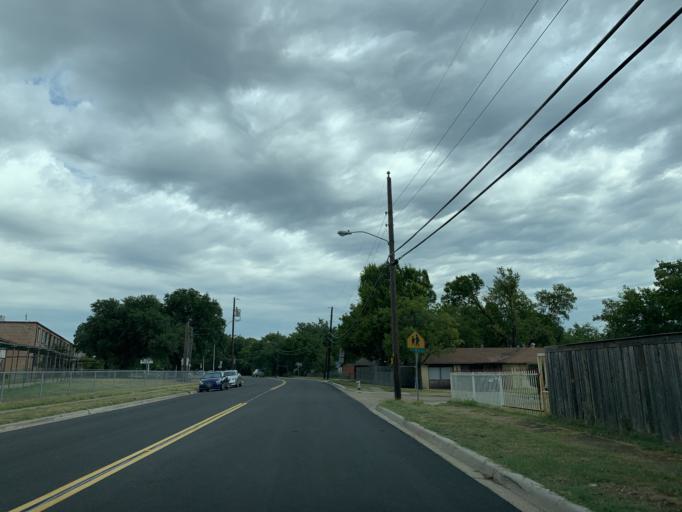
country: US
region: Texas
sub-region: Dallas County
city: Duncanville
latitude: 32.6648
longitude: -96.8298
